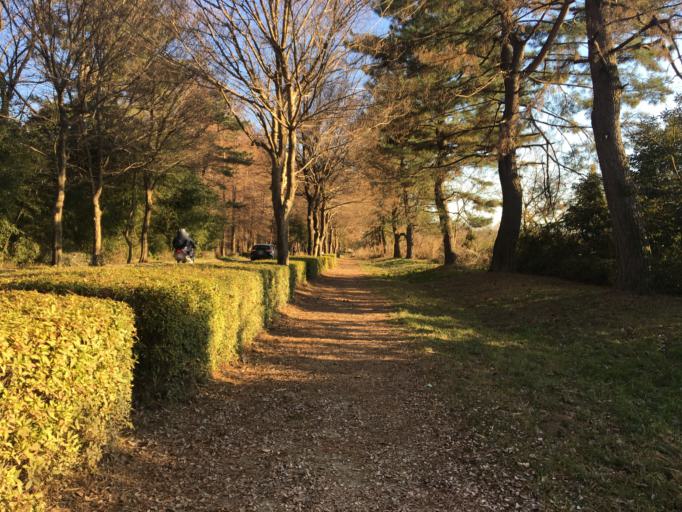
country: JP
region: Saitama
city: Shiki
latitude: 35.8448
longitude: 139.6061
